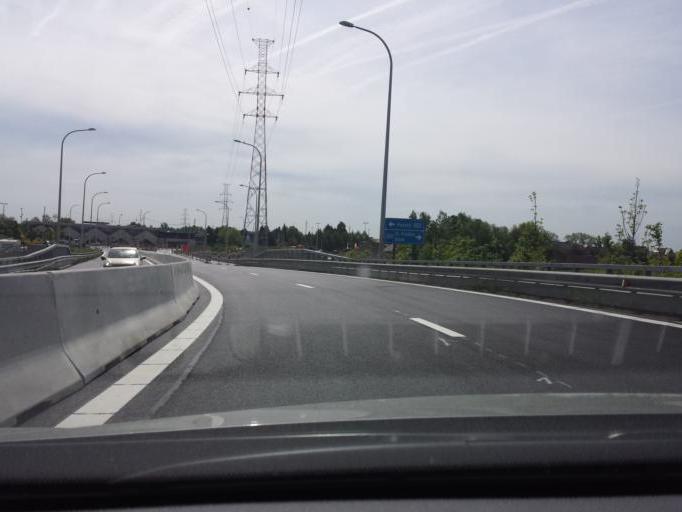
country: BE
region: Flanders
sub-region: Provincie Limburg
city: Hasselt
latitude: 50.9157
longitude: 5.3210
